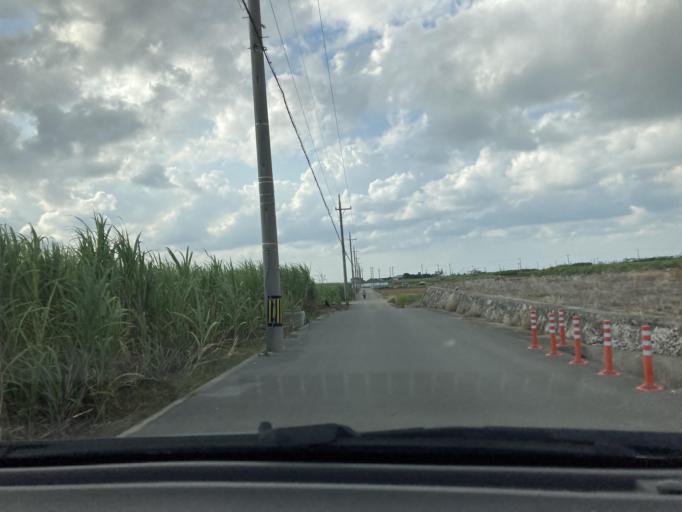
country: JP
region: Okinawa
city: Itoman
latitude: 26.0825
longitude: 127.6686
